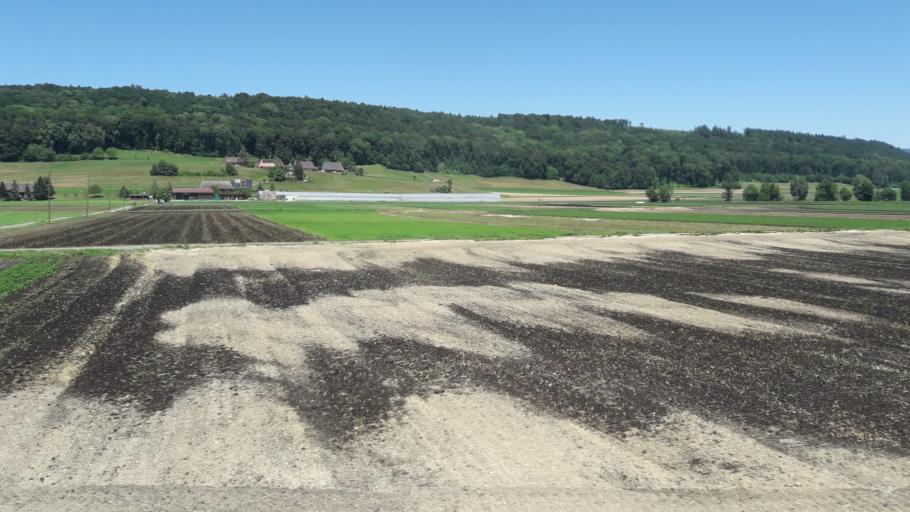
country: CH
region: Bern
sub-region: Seeland District
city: Tauffelen
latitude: 47.0258
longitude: 7.1638
